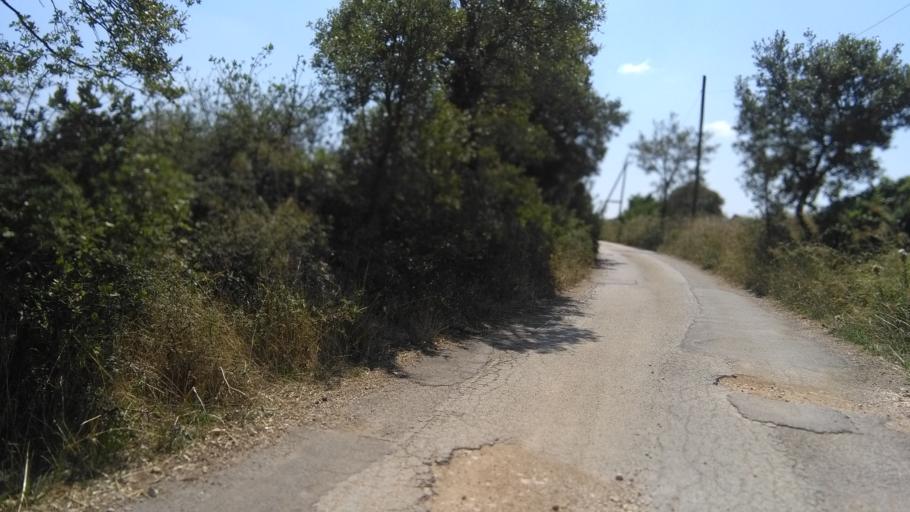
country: IT
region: Apulia
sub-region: Provincia di Bari
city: Noci
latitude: 40.8104
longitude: 17.1810
